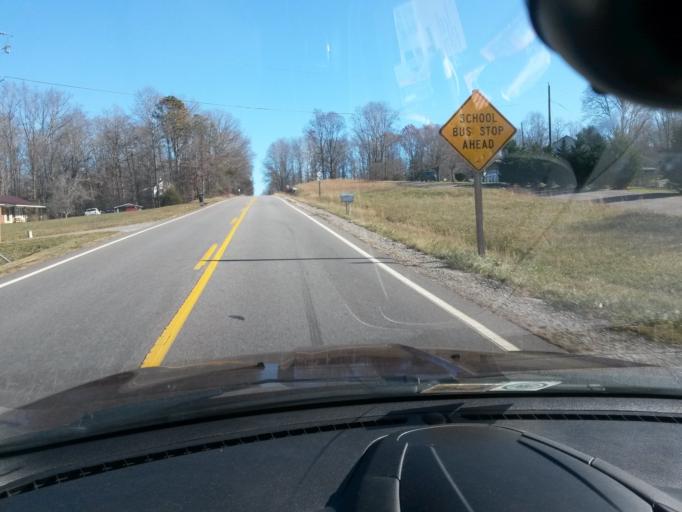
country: US
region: Virginia
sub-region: Patrick County
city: Patrick Springs
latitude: 36.7739
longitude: -80.1423
